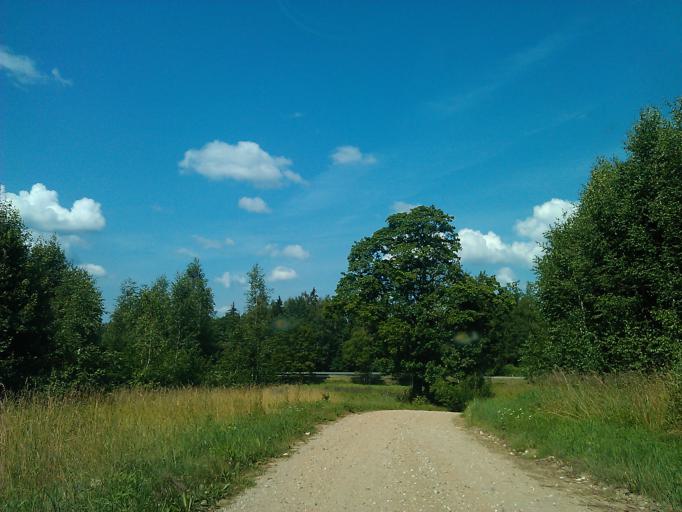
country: LV
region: Amatas Novads
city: Drabesi
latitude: 57.2489
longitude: 25.2625
